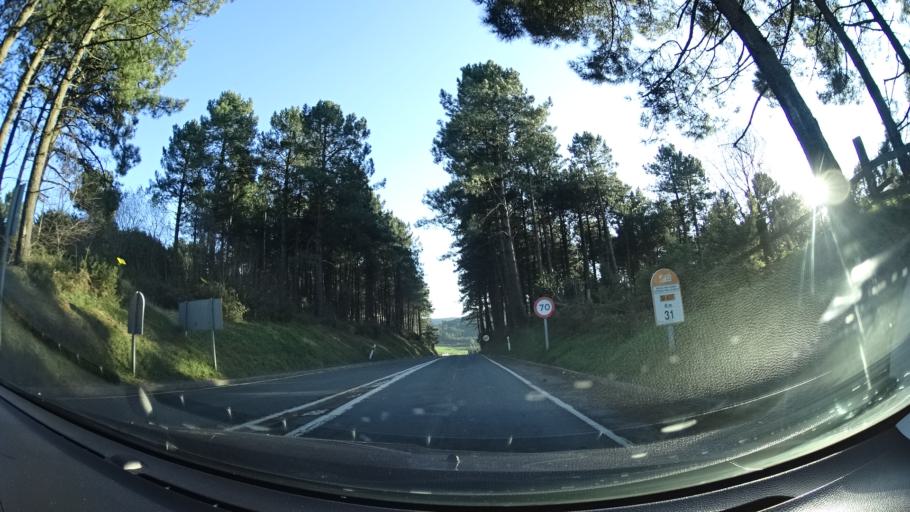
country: ES
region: Basque Country
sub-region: Bizkaia
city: Bermeo
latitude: 43.4045
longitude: -2.7605
